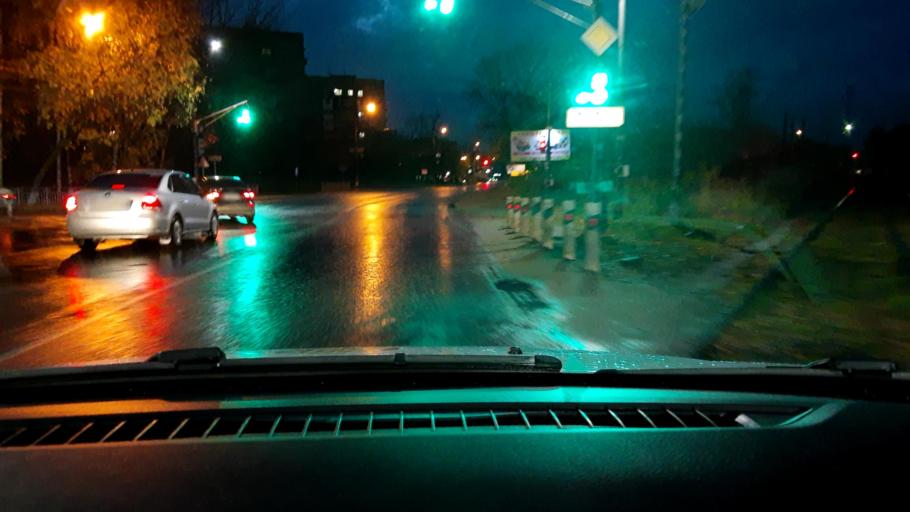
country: RU
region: Nizjnij Novgorod
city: Bor
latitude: 56.3535
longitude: 44.0755
